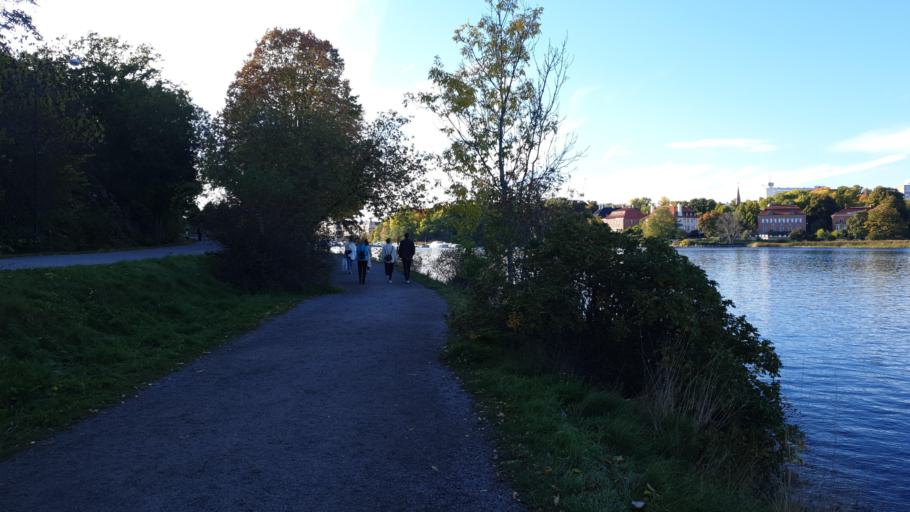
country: SE
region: Stockholm
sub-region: Stockholms Kommun
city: OEstermalm
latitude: 59.3293
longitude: 18.1080
